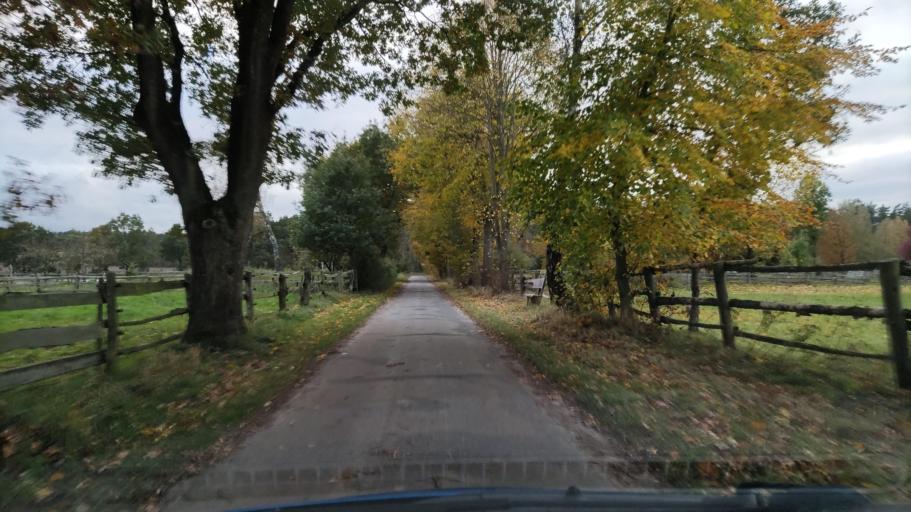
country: DE
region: Lower Saxony
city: Karwitz
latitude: 53.1282
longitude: 10.9954
